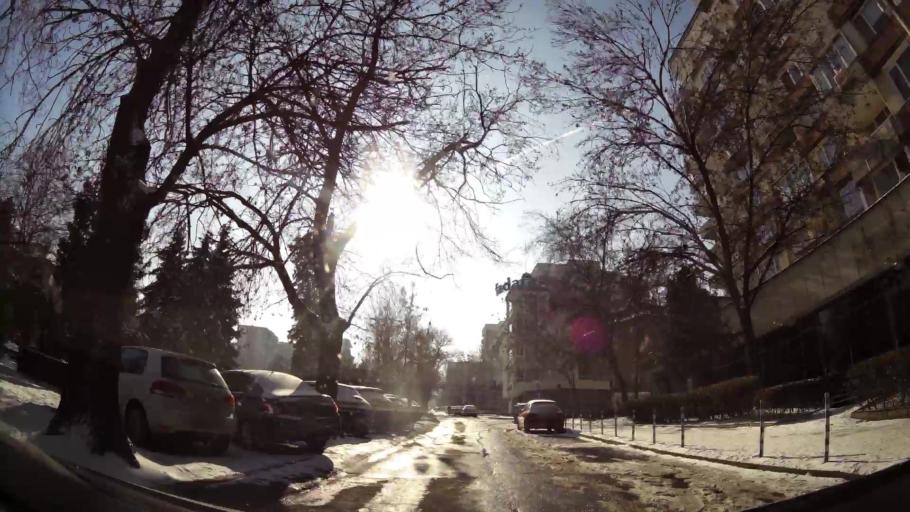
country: BG
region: Sofia-Capital
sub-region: Stolichna Obshtina
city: Sofia
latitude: 42.6762
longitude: 23.3215
